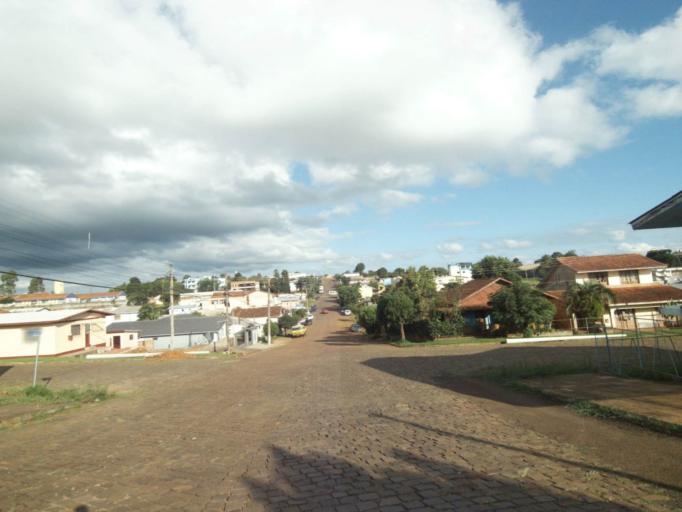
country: BR
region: Rio Grande do Sul
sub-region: Lagoa Vermelha
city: Lagoa Vermelha
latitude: -28.2031
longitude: -51.5230
